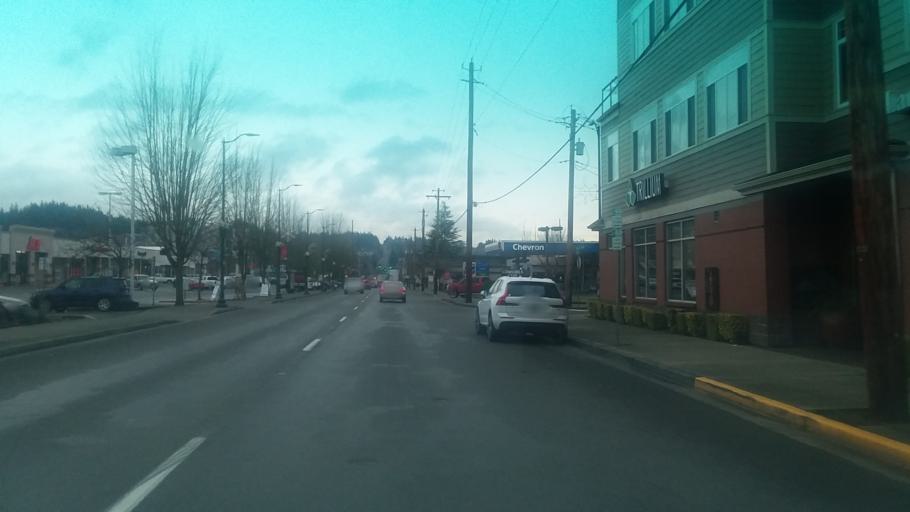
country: US
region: Washington
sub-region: Pierce County
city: Puyallup
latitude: 47.1884
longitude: -122.2938
